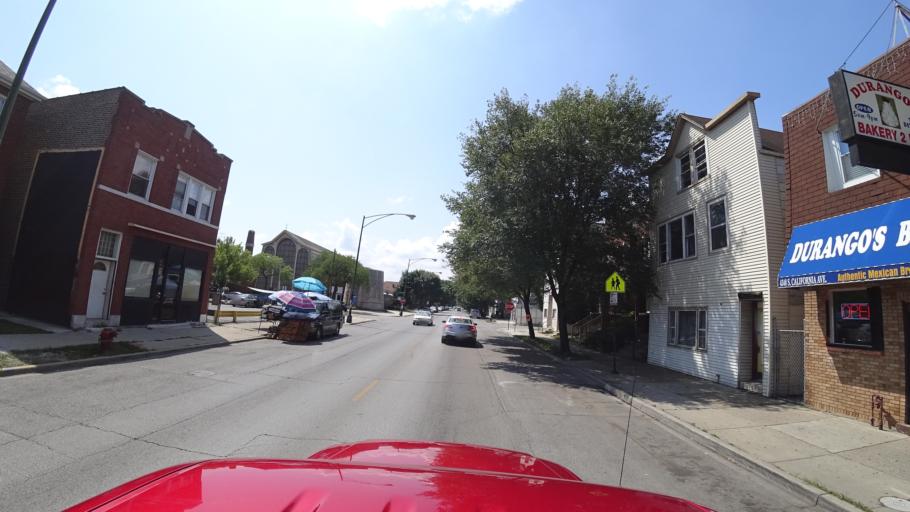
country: US
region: Illinois
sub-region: Cook County
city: Chicago
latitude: 41.8143
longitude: -87.6944
